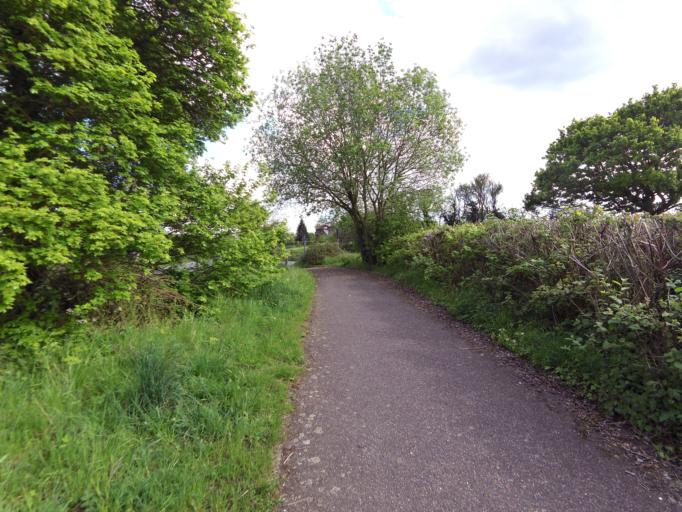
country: GB
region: England
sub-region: Suffolk
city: Woolpit
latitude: 52.2179
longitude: 0.9002
